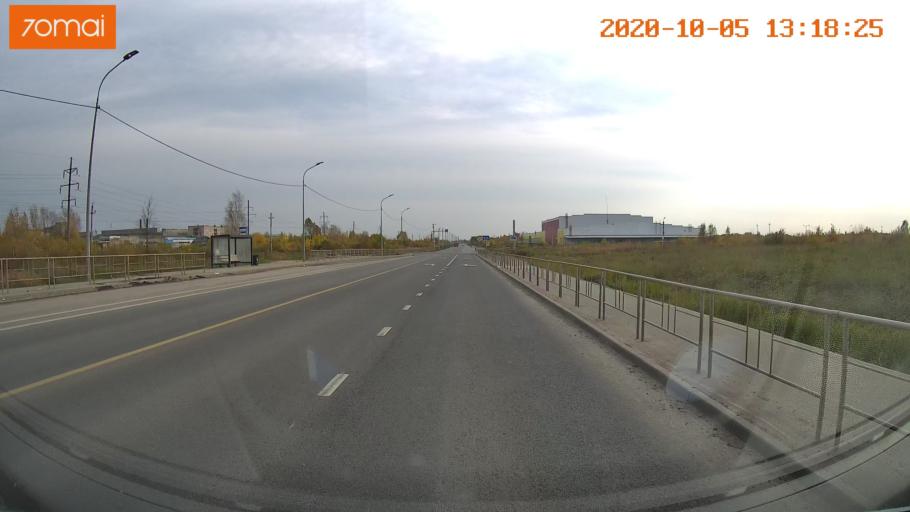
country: RU
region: Ivanovo
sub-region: Gorod Ivanovo
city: Ivanovo
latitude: 56.9773
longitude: 40.9201
